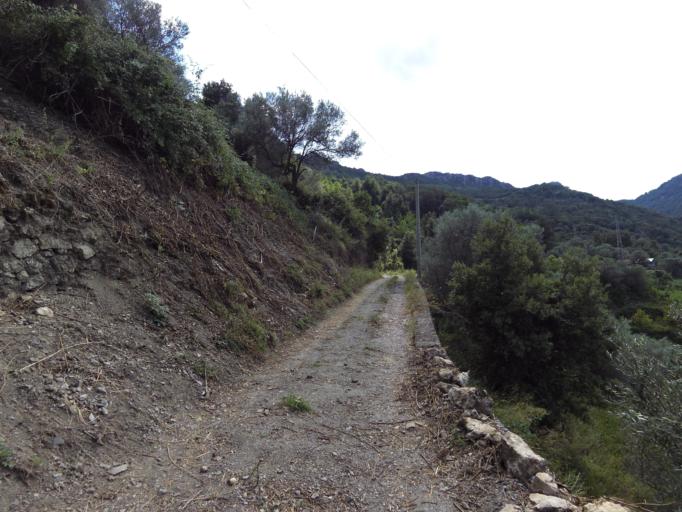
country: IT
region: Calabria
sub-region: Provincia di Reggio Calabria
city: Pazzano
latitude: 38.4742
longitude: 16.4425
